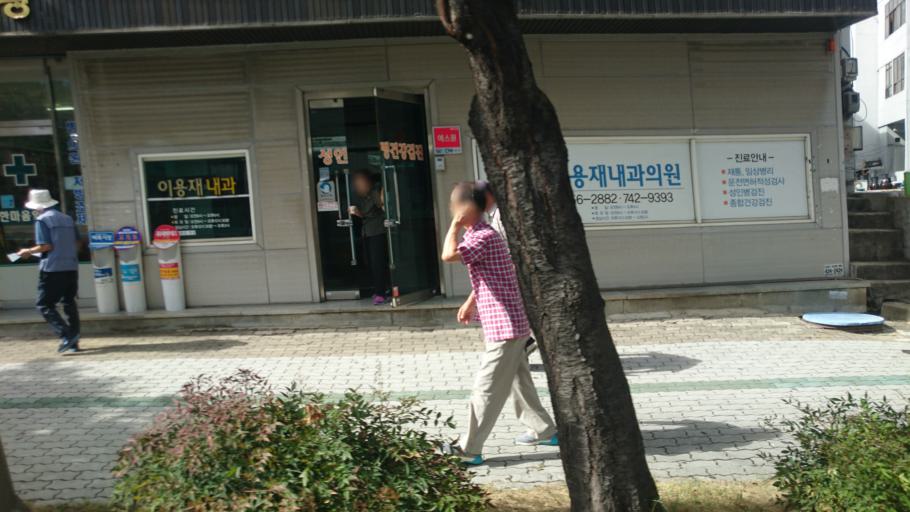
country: KR
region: Daegu
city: Daegu
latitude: 35.8732
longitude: 128.6389
